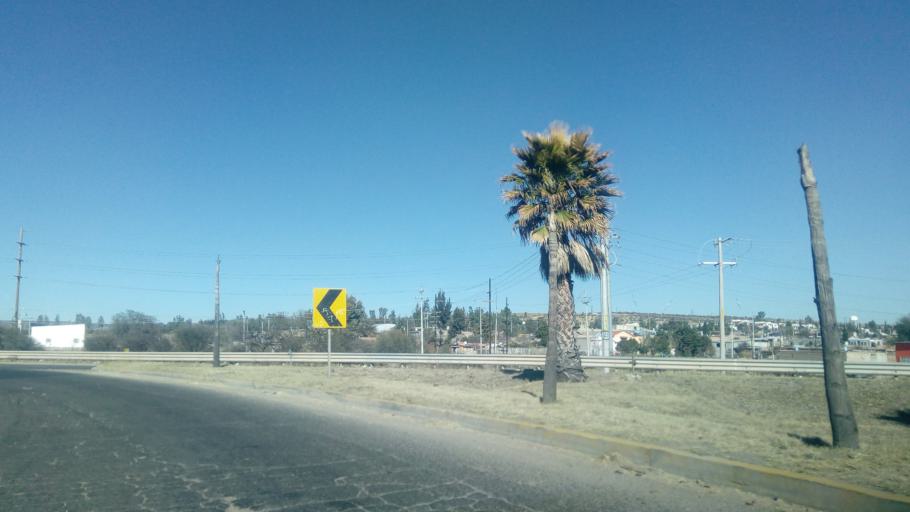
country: MX
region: Durango
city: Victoria de Durango
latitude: 24.0961
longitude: -104.5741
